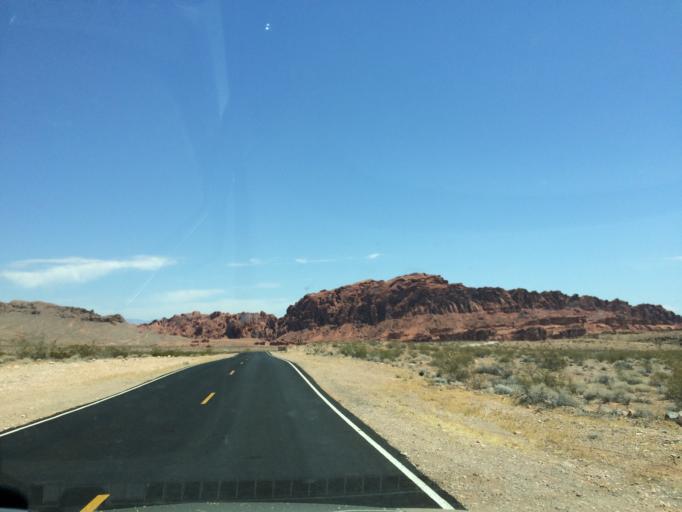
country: US
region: Nevada
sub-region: Clark County
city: Moapa Valley
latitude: 36.4193
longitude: -114.5450
